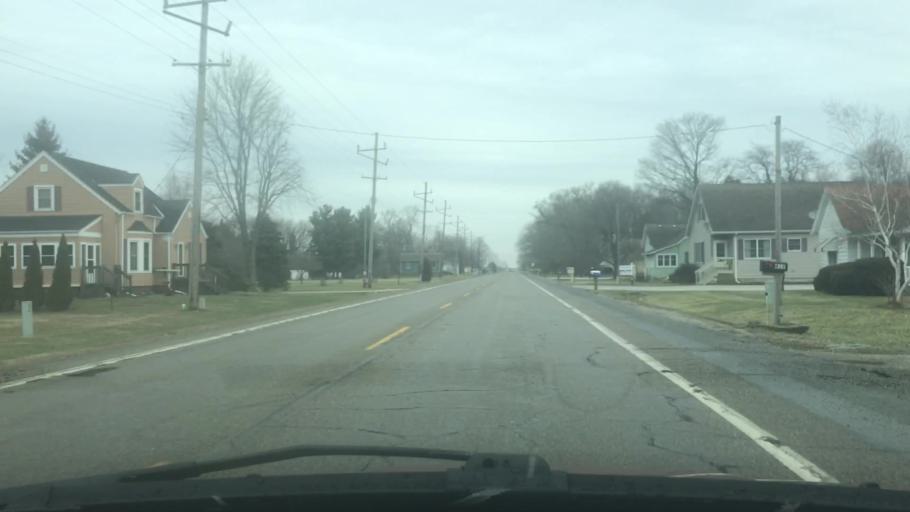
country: US
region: Indiana
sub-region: Porter County
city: Kouts
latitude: 41.3217
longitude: -87.0259
